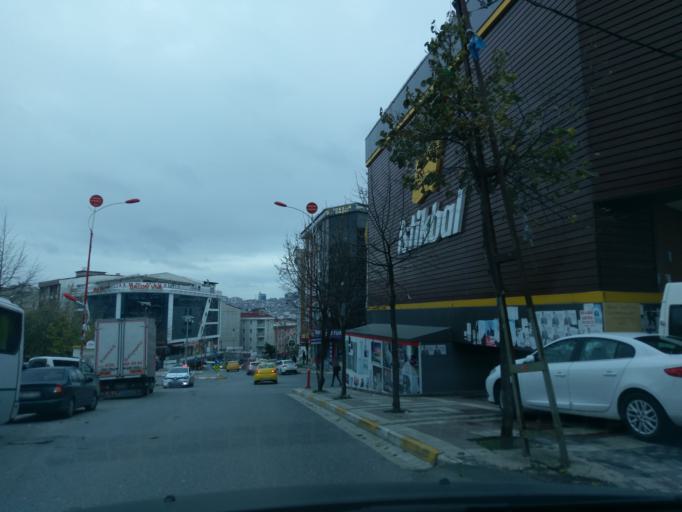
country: TR
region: Istanbul
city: Esenyurt
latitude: 41.0175
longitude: 28.6647
